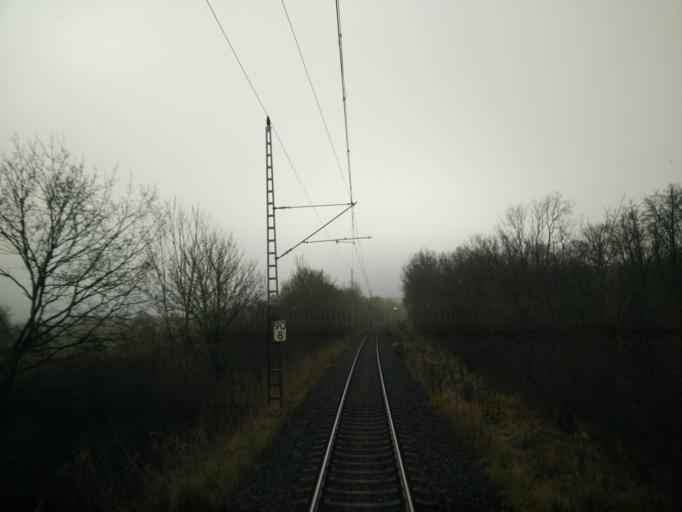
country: DE
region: Mecklenburg-Vorpommern
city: Mecklenburg
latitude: 53.8322
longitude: 11.4783
